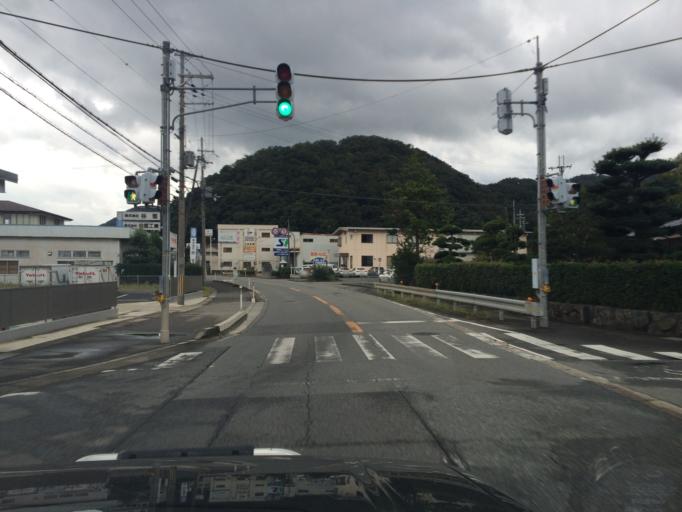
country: JP
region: Hyogo
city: Toyooka
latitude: 35.4562
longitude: 134.7725
